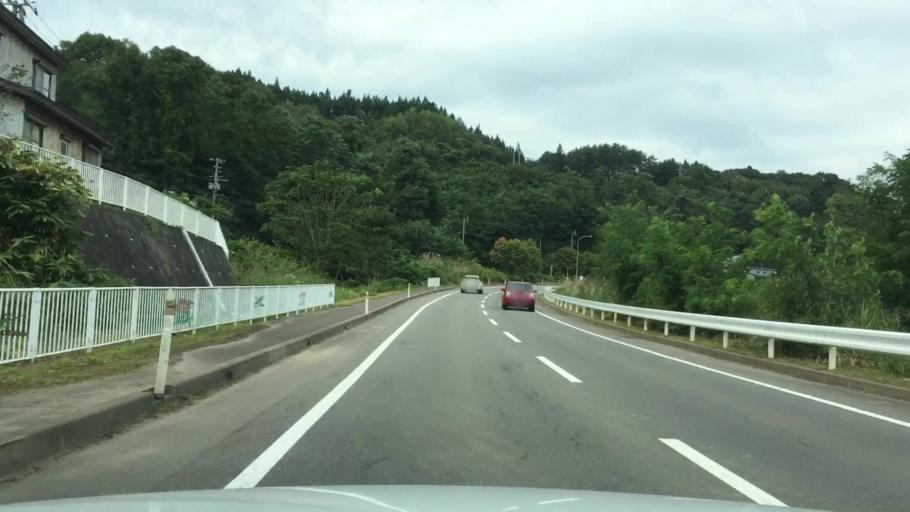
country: JP
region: Aomori
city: Shimokizukuri
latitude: 40.7615
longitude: 140.2266
